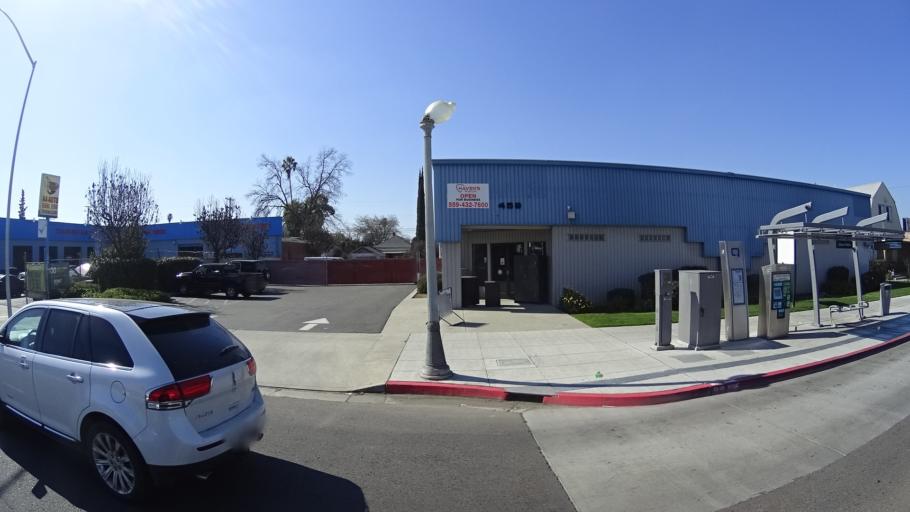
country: US
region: California
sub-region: Fresno County
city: Fresno
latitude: 36.7497
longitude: -119.7906
